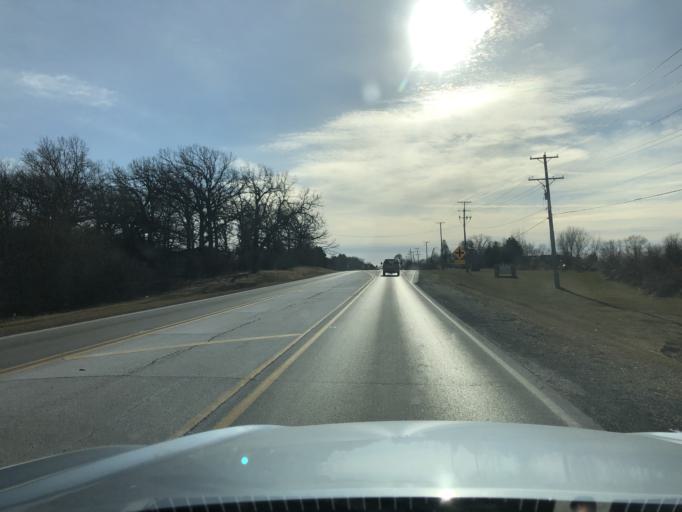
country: US
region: Illinois
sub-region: Lake County
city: Grandwood Park
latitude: 42.4040
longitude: -88.0041
